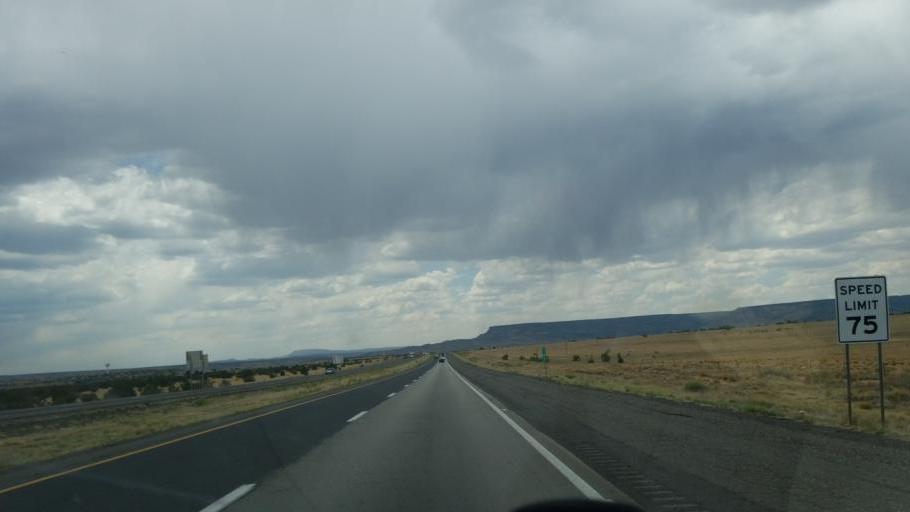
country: US
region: New Mexico
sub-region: Cibola County
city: Skyline-Ganipa
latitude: 35.0748
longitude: -107.5766
